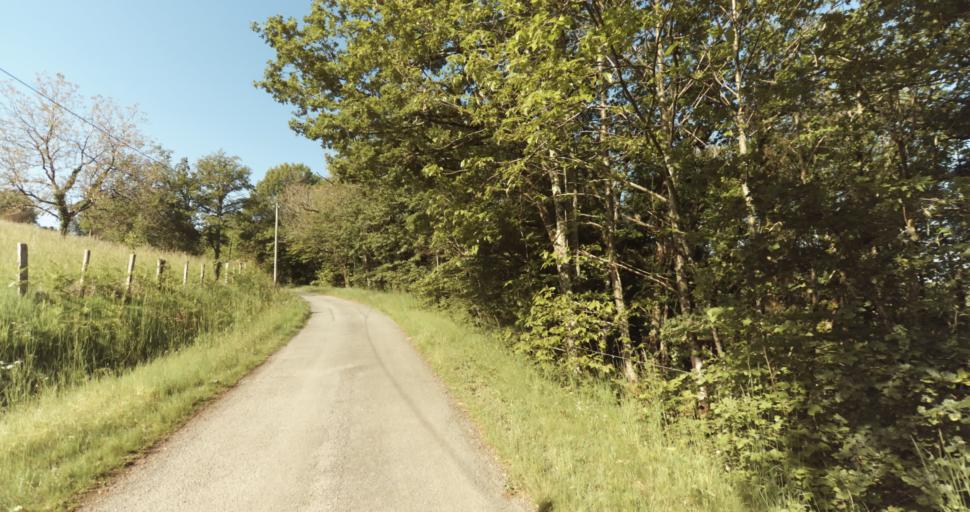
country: FR
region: Limousin
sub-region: Departement de la Haute-Vienne
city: Solignac
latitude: 45.7344
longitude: 1.2438
